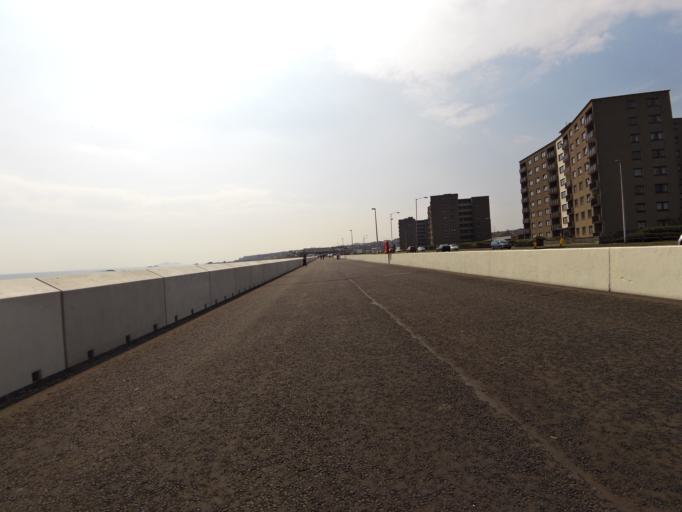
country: GB
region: Scotland
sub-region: Fife
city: Kirkcaldy
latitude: 56.1024
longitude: -3.1592
